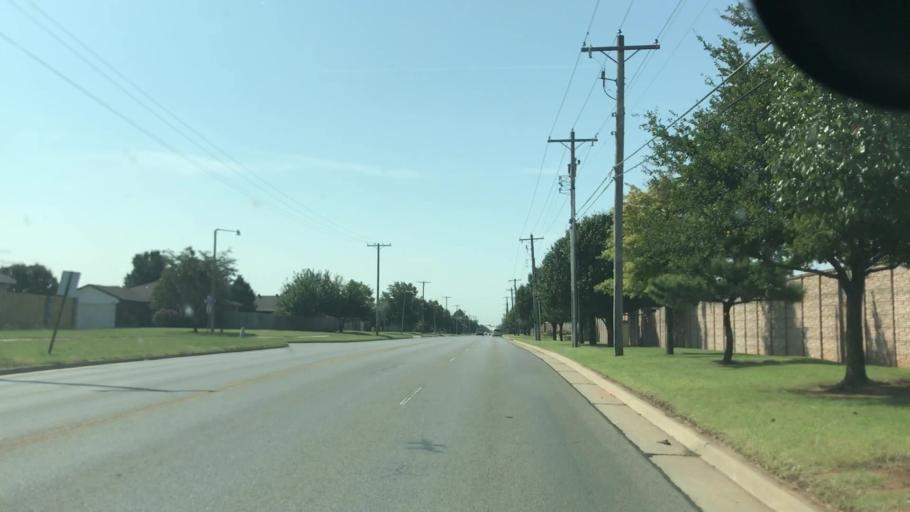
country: US
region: Oklahoma
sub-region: Cleveland County
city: Moore
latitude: 35.3555
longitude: -97.5122
